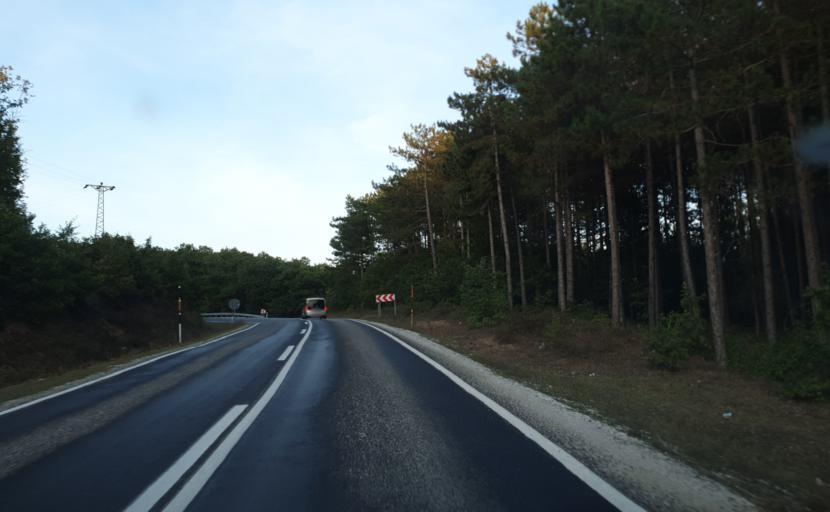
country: TR
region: Kirklareli
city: Igneada
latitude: 41.8588
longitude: 27.8124
